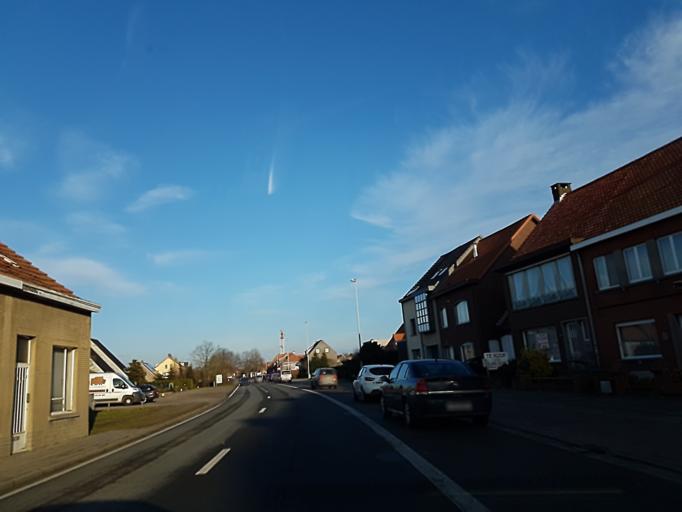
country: BE
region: Flanders
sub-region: Provincie Antwerpen
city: Turnhout
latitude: 51.3348
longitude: 4.9653
